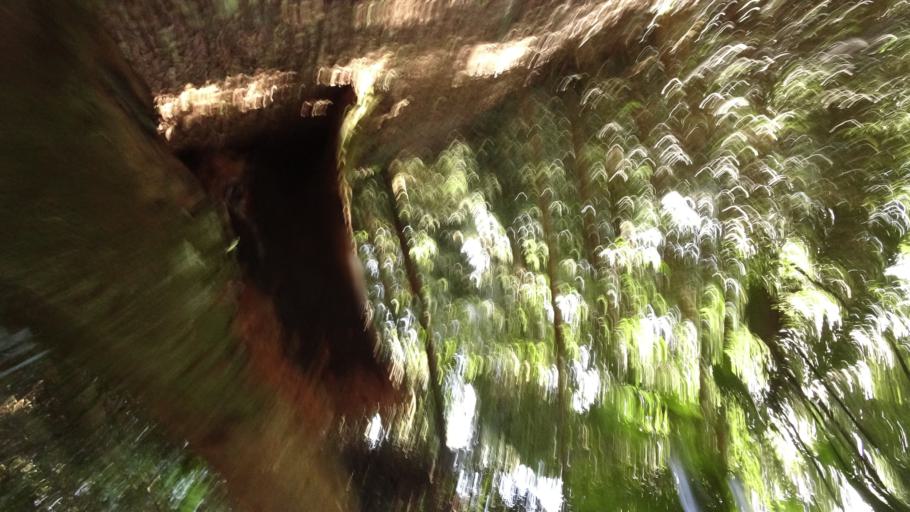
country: AU
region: Queensland
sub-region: Moreton Bay
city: Highvale
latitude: -27.4054
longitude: 152.8119
